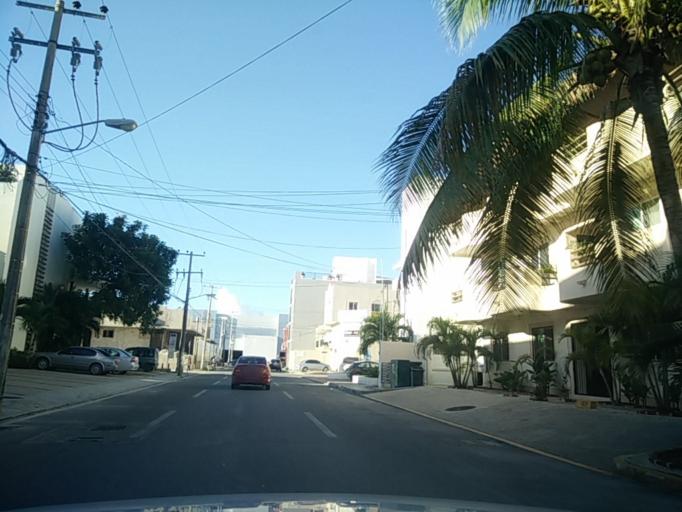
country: MX
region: Quintana Roo
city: Playa del Carmen
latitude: 20.6333
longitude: -87.0728
